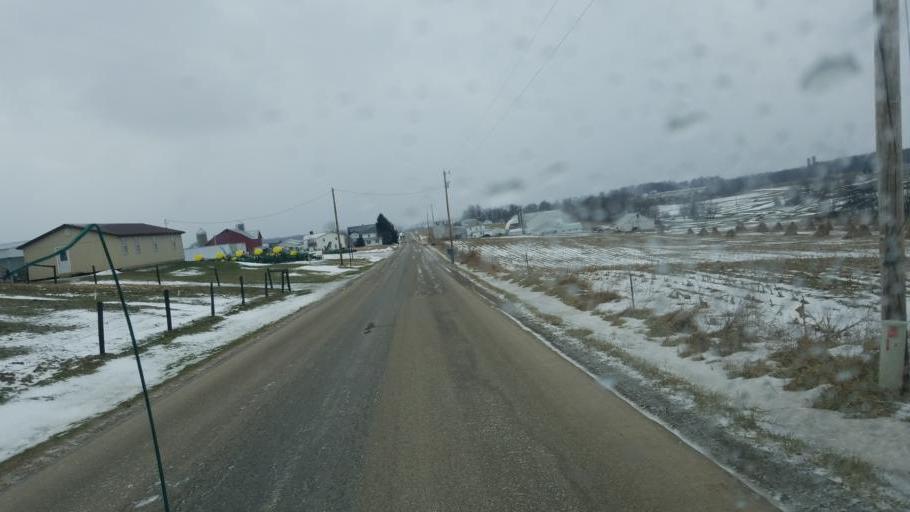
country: US
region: Ohio
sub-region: Wayne County
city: Apple Creek
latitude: 40.6753
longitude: -81.8004
